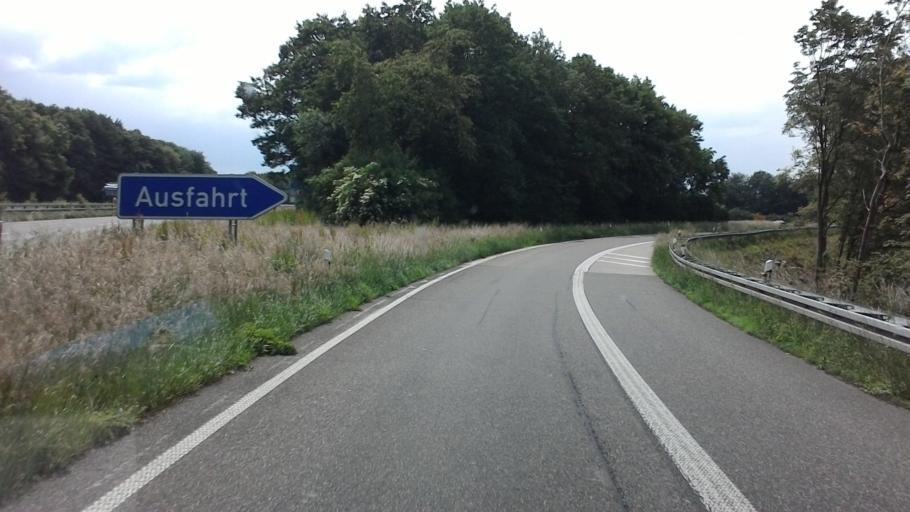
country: BE
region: Wallonia
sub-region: Province de Liege
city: Raeren
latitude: 50.7233
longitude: 6.1288
